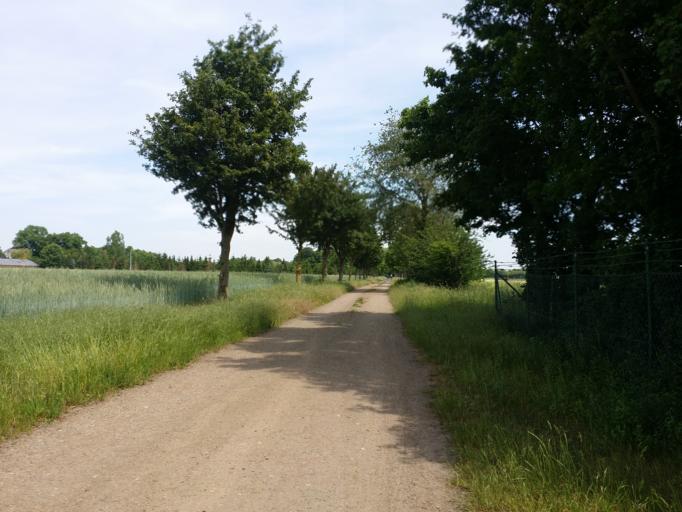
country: DE
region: Lower Saxony
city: Syke
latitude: 52.9746
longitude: 8.8662
